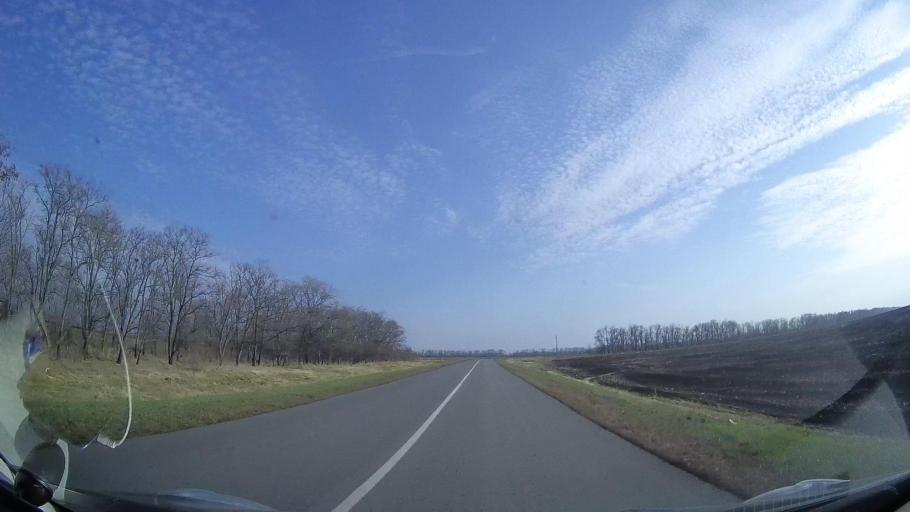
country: RU
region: Rostov
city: Mechetinskaya
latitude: 46.9043
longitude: 40.5391
